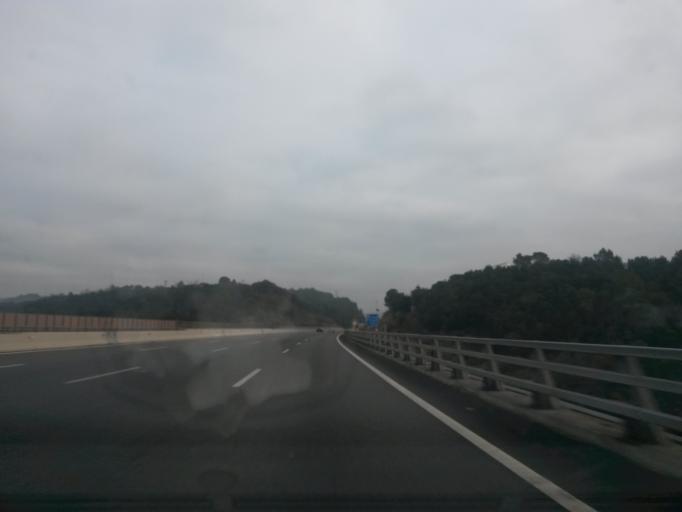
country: ES
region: Catalonia
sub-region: Provincia de Girona
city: Sarria de Ter
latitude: 42.0085
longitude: 2.8088
